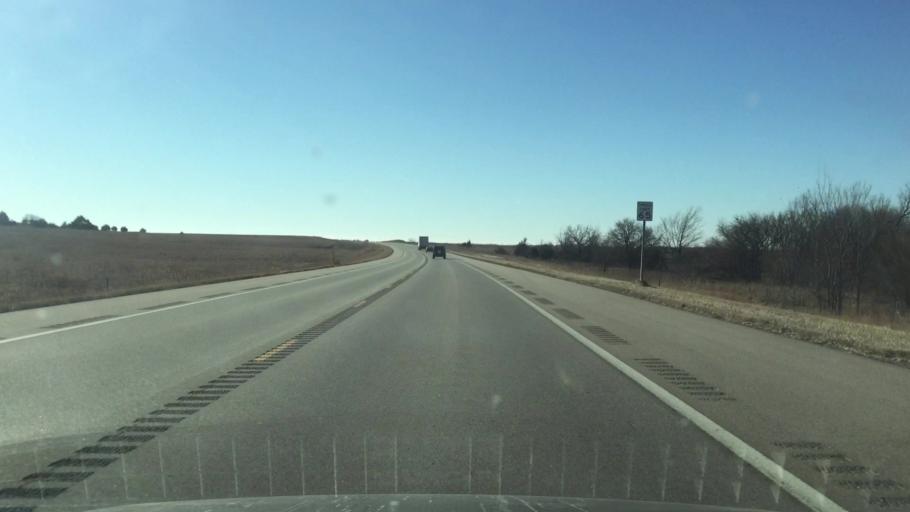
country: US
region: Kansas
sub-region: Allen County
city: Iola
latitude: 38.0656
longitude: -95.3798
